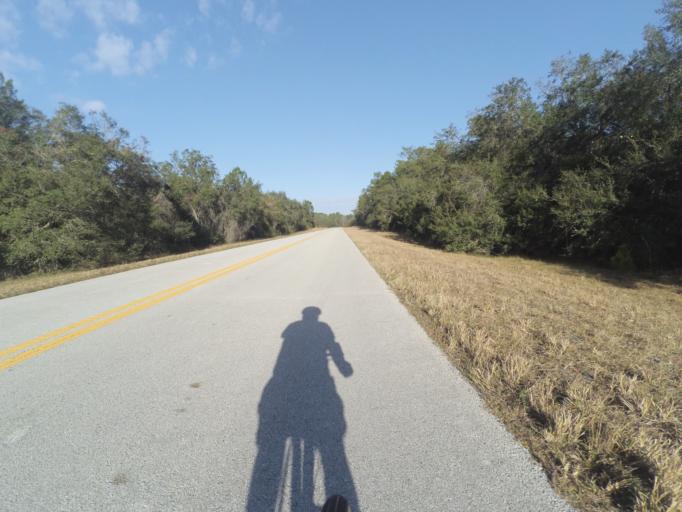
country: US
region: Florida
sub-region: Lake County
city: Astor
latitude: 29.1111
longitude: -81.5711
